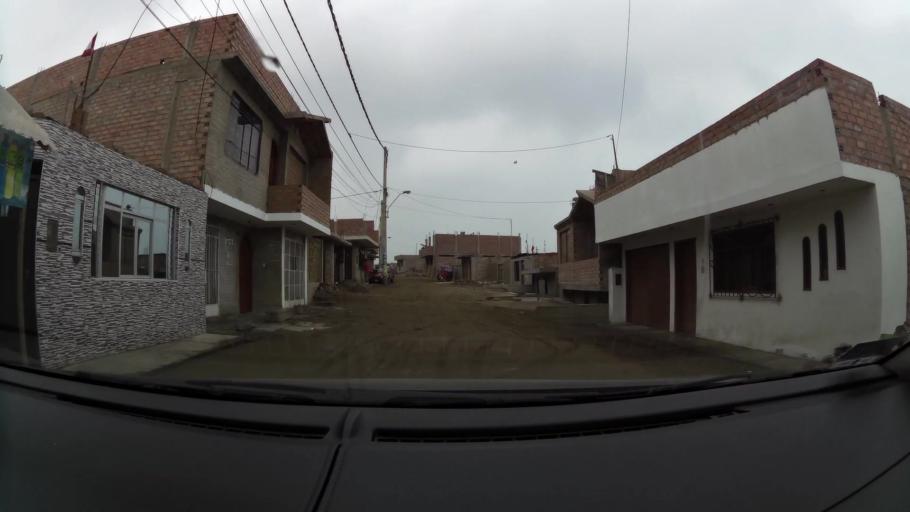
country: PE
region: Lima
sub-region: Provincia de Huaral
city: Chancay
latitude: -11.5872
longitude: -77.2673
